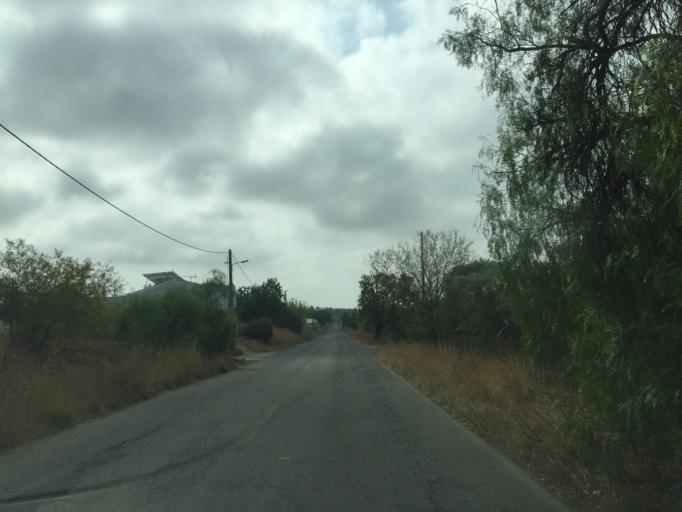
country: PT
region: Faro
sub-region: Olhao
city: Olhao
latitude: 37.0691
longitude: -7.8819
